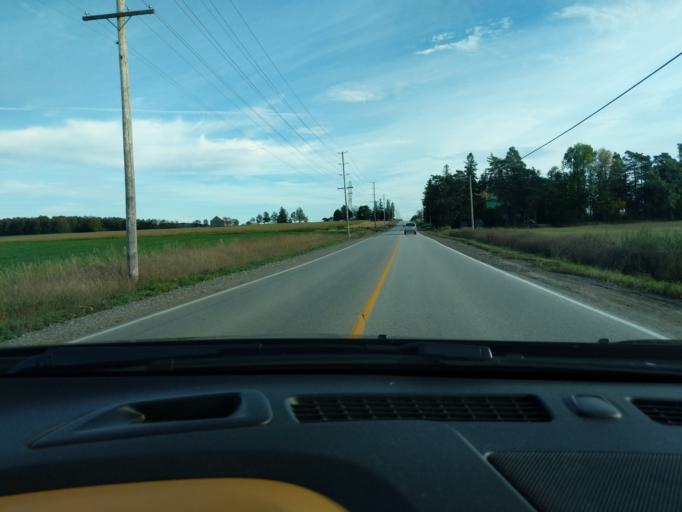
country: CA
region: Ontario
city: Barrie
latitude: 44.4125
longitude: -79.7518
